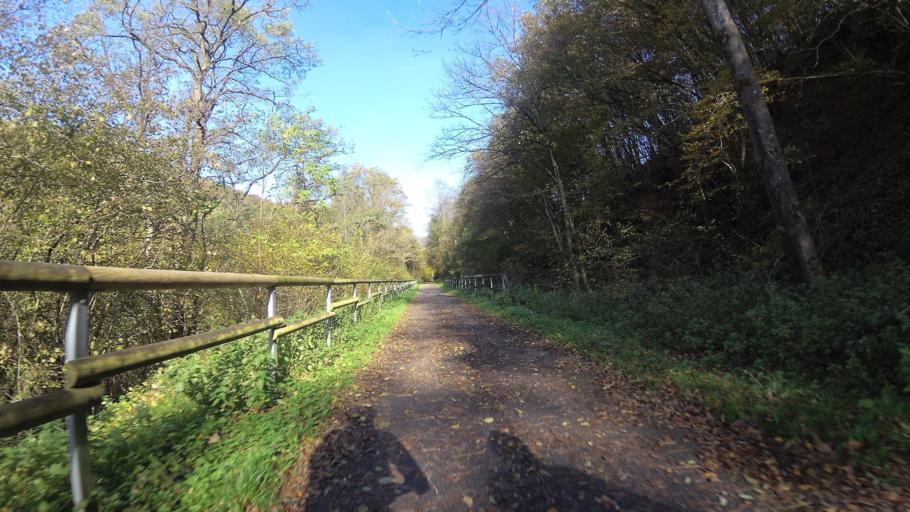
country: DE
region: Rheinland-Pfalz
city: Morscheid
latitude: 49.7343
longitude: 6.7422
